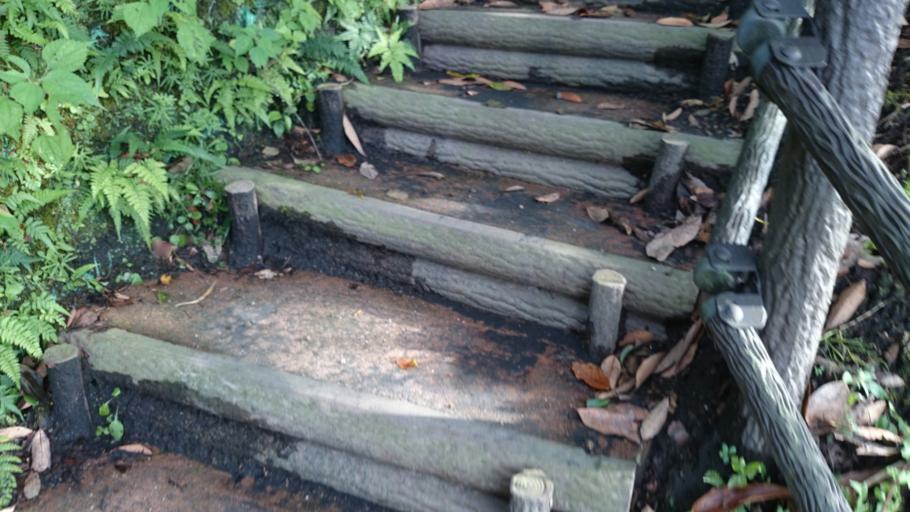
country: JP
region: Kagoshima
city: Tarumizu
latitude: 31.5555
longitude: 130.7343
